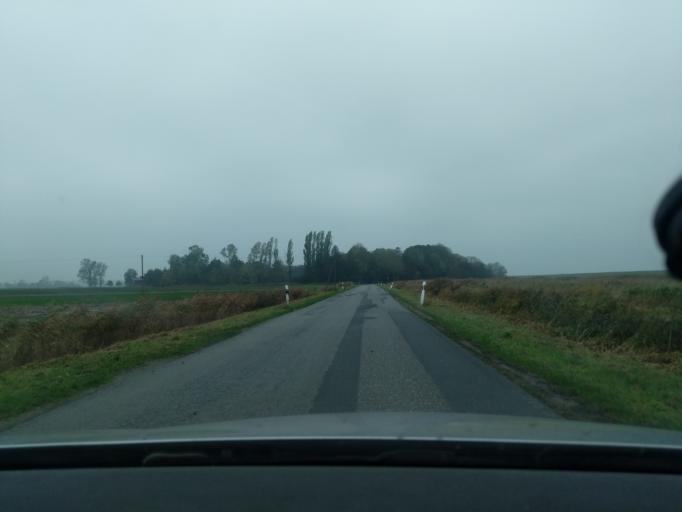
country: DE
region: Lower Saxony
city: Nordleda
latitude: 53.8262
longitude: 8.8304
